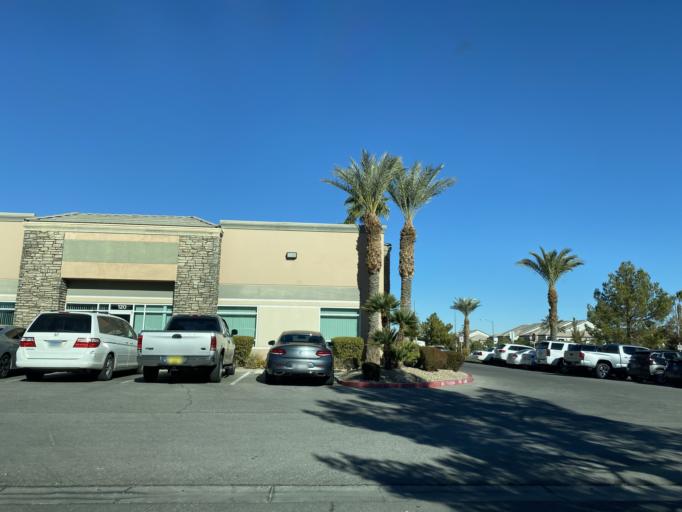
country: US
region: Nevada
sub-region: Clark County
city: Spring Valley
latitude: 36.0676
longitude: -115.2521
